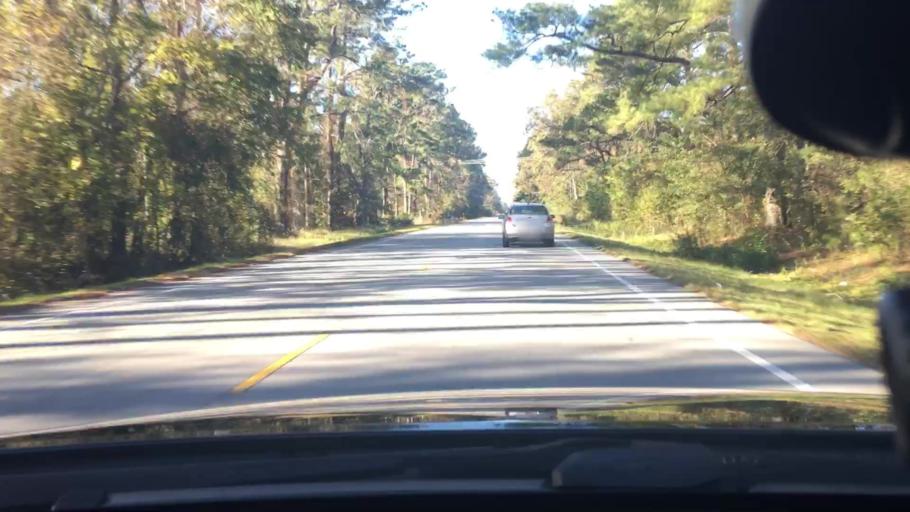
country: US
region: North Carolina
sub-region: Craven County
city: New Bern
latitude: 35.1620
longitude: -77.0390
